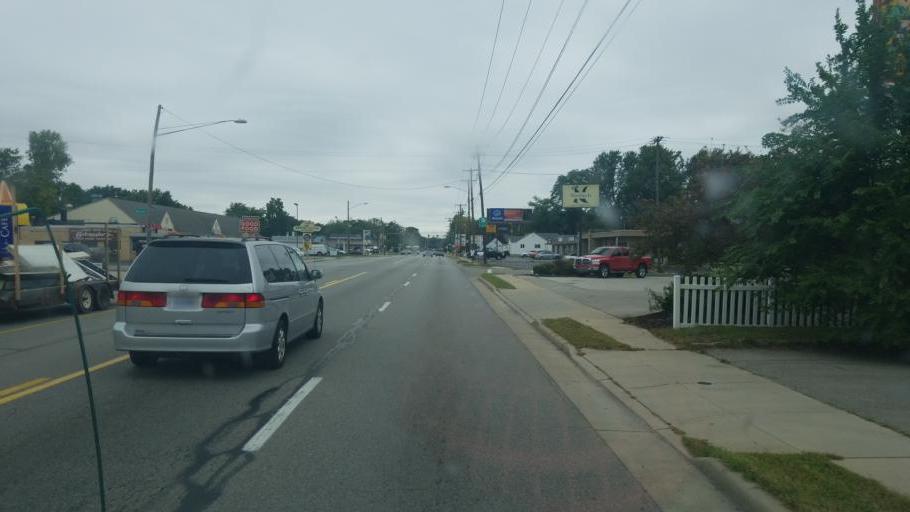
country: US
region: Ohio
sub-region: Lucas County
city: Ottawa Hills
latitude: 41.6599
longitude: -83.6675
